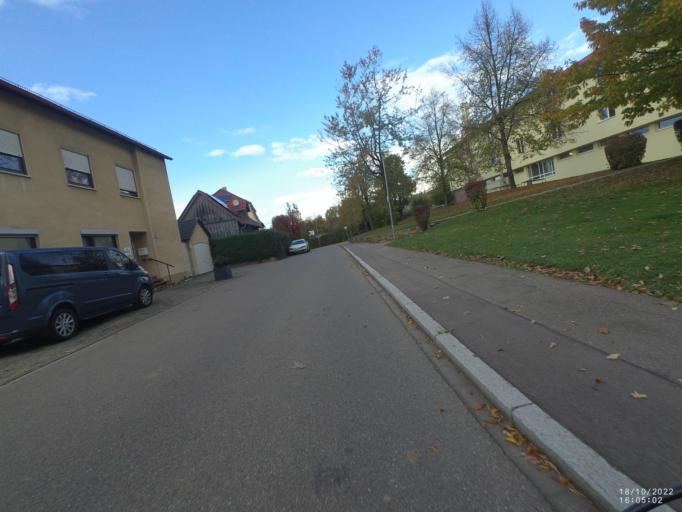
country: DE
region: Baden-Wuerttemberg
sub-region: Regierungsbezirk Stuttgart
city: Salach
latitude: 48.6930
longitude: 9.7449
